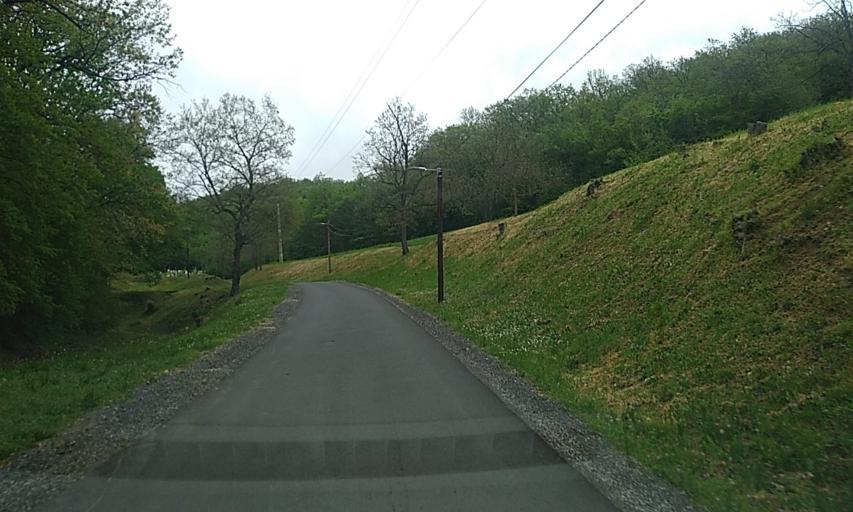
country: RS
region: Central Serbia
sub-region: Nisavski Okrug
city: Razanj
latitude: 43.6206
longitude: 21.5267
